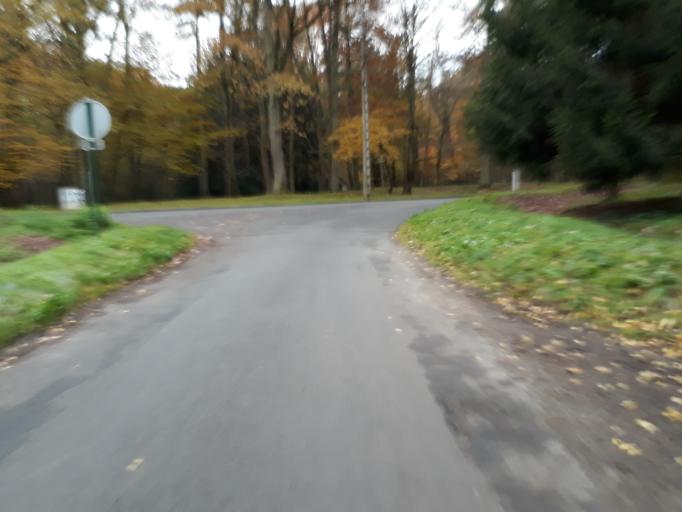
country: FR
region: Ile-de-France
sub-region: Departement de Seine-et-Marne
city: Bois-le-Roi
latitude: 48.4624
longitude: 2.6990
